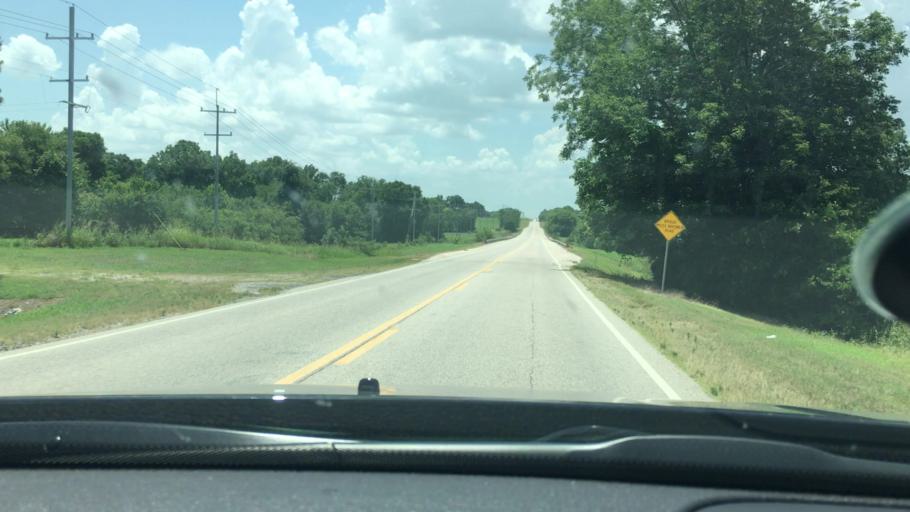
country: US
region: Oklahoma
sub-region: Pontotoc County
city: Ada
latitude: 34.6883
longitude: -96.6349
